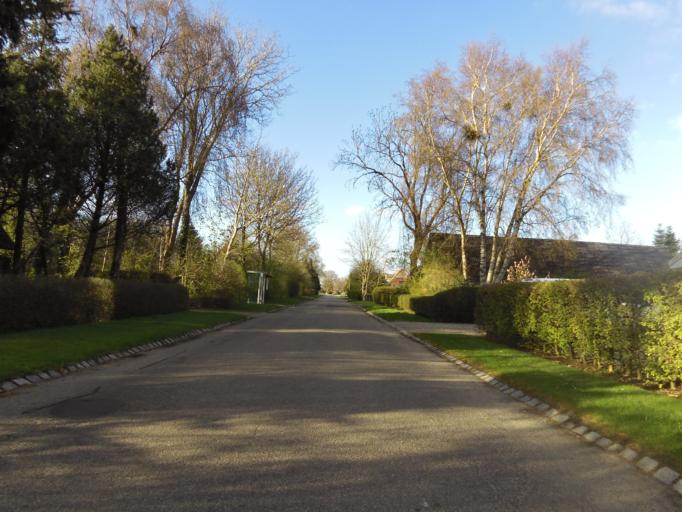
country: DK
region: South Denmark
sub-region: Tonder Kommune
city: Toftlund
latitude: 55.2317
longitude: 9.1235
